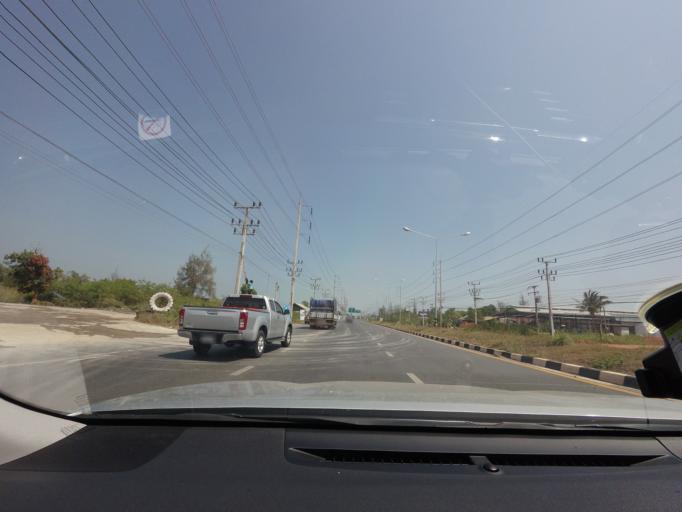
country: TH
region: Surat Thani
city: Surat Thani
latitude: 9.1604
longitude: 99.3710
